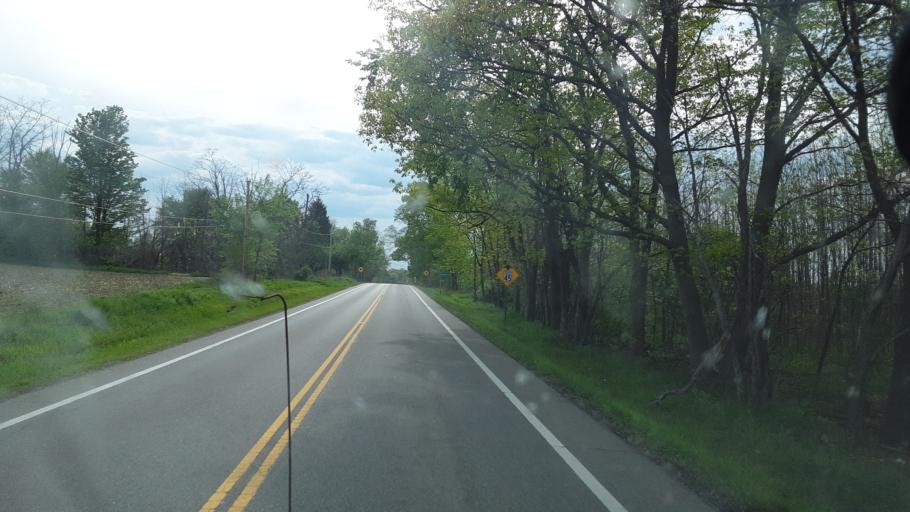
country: US
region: Ohio
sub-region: Portage County
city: Garrettsville
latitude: 41.2356
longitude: -81.1299
